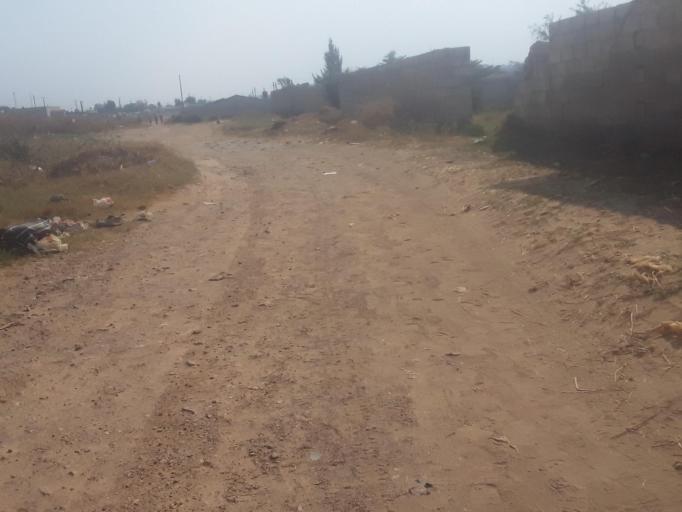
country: ZM
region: Lusaka
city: Lusaka
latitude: -15.3710
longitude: 28.2949
